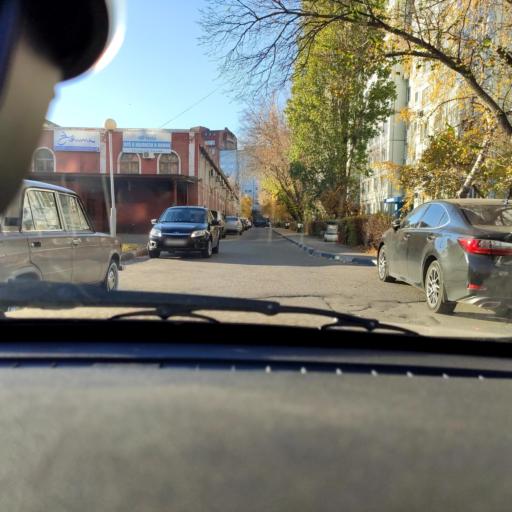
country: RU
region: Samara
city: Tol'yatti
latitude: 53.5284
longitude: 49.3260
